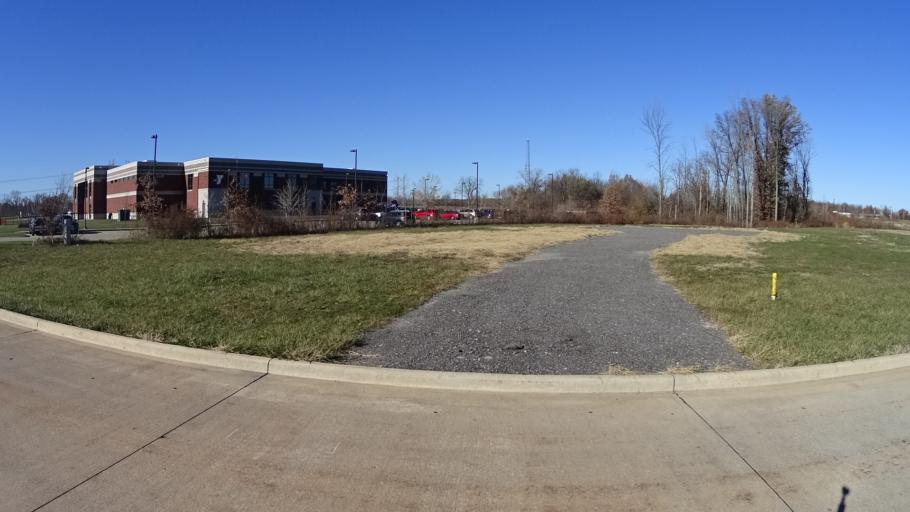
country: US
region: Ohio
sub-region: Lorain County
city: Avon
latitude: 41.4611
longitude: -82.0601
